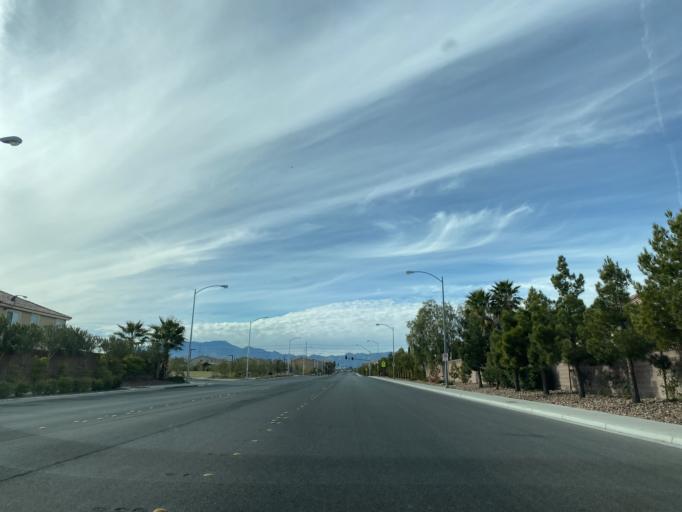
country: US
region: Nevada
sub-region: Clark County
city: Enterprise
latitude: 36.0344
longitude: -115.2359
